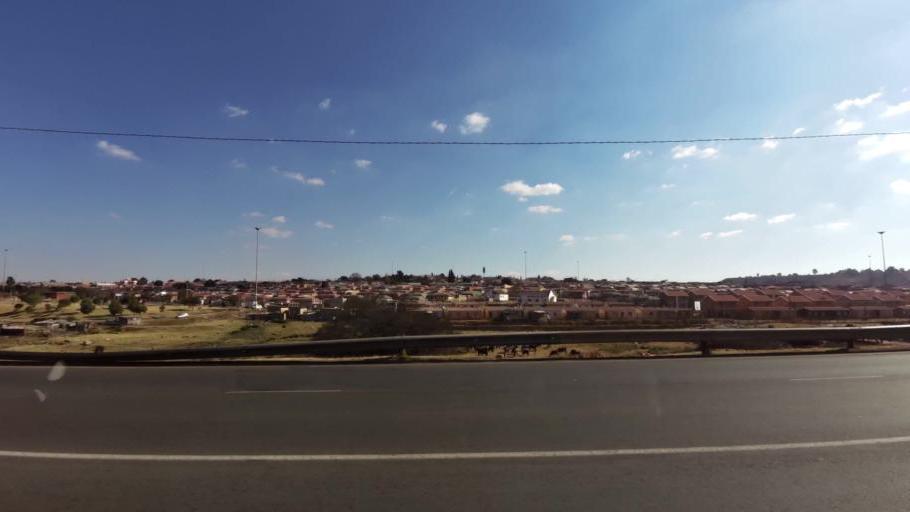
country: ZA
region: Gauteng
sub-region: City of Johannesburg Metropolitan Municipality
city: Soweto
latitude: -26.2281
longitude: 27.9240
